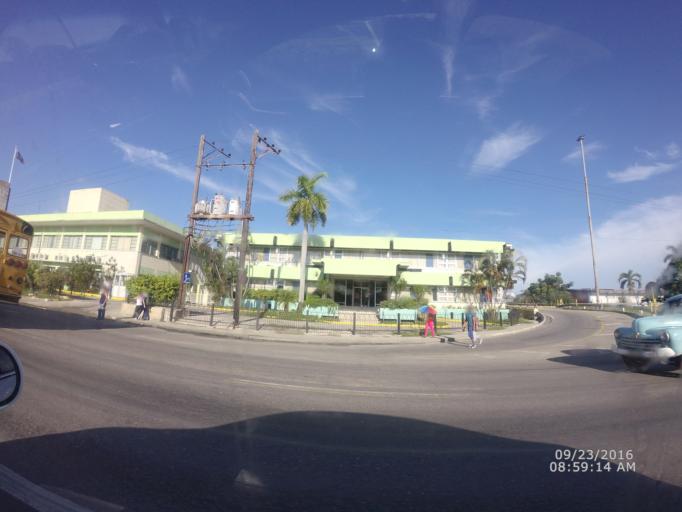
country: CU
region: La Habana
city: Diez de Octubre
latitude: 23.0721
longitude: -82.3983
